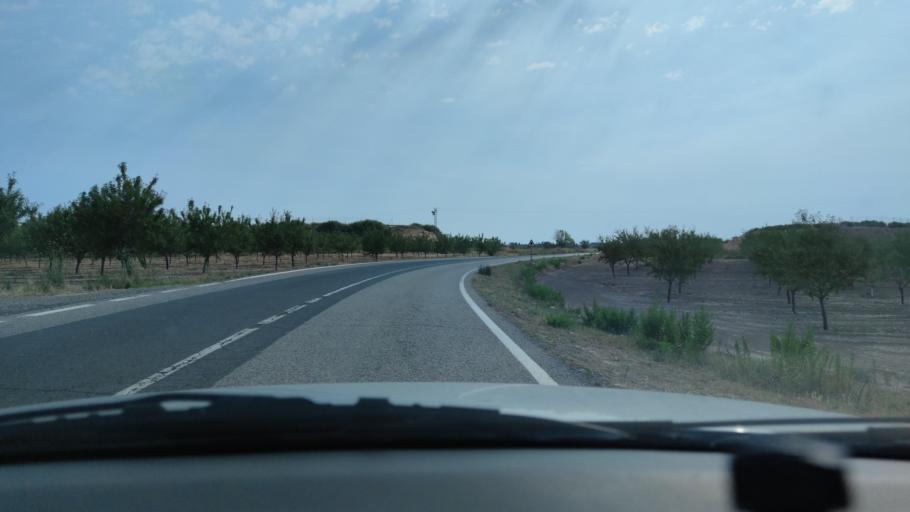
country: ES
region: Catalonia
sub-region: Provincia de Lleida
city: Arbeca
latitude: 41.5030
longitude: 0.9479
